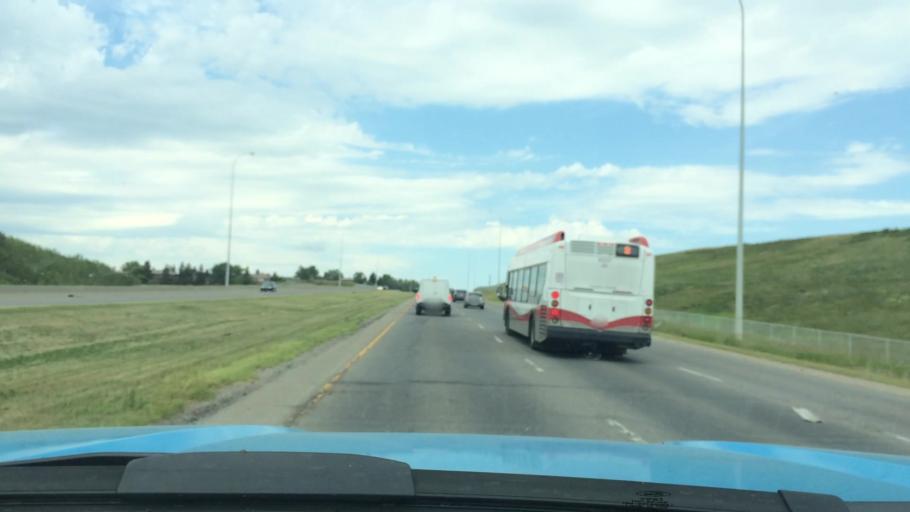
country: CA
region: Alberta
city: Calgary
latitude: 51.1187
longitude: -114.1339
